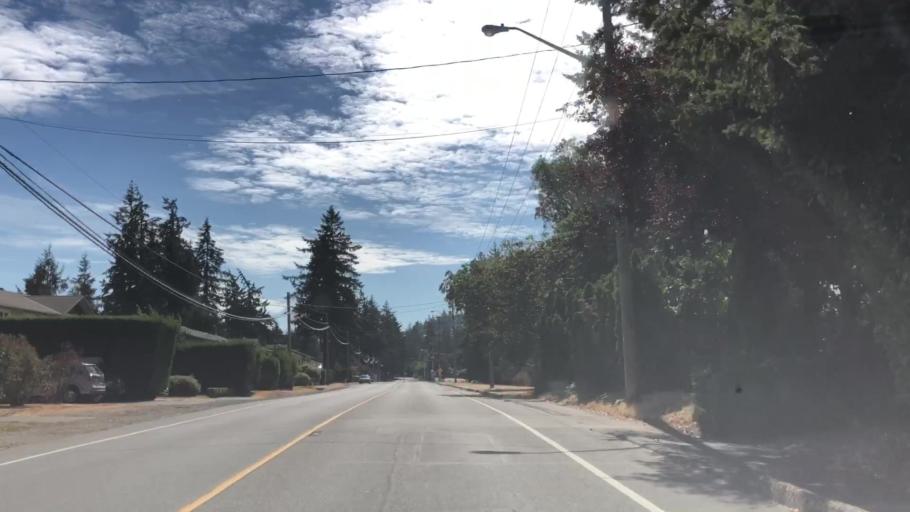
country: CA
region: British Columbia
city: Colwood
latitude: 48.4243
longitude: -123.4917
